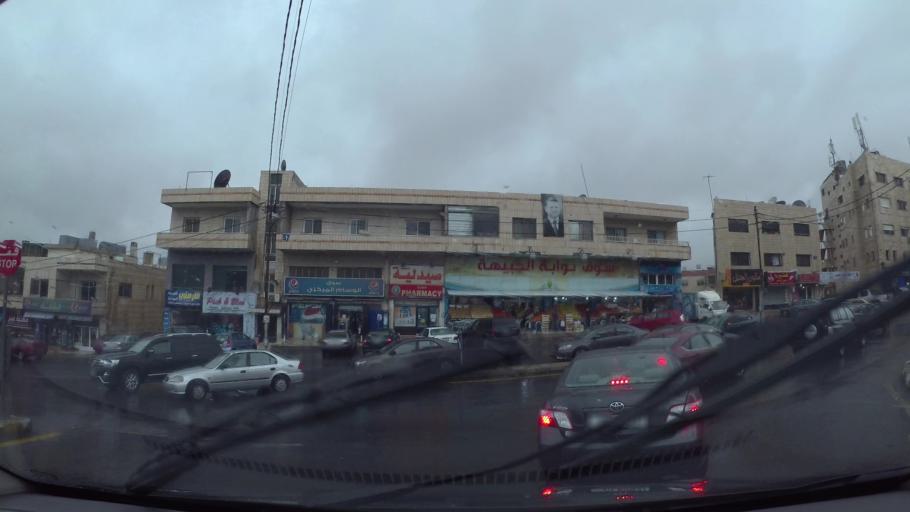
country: JO
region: Amman
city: Al Jubayhah
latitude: 32.0231
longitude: 35.8744
